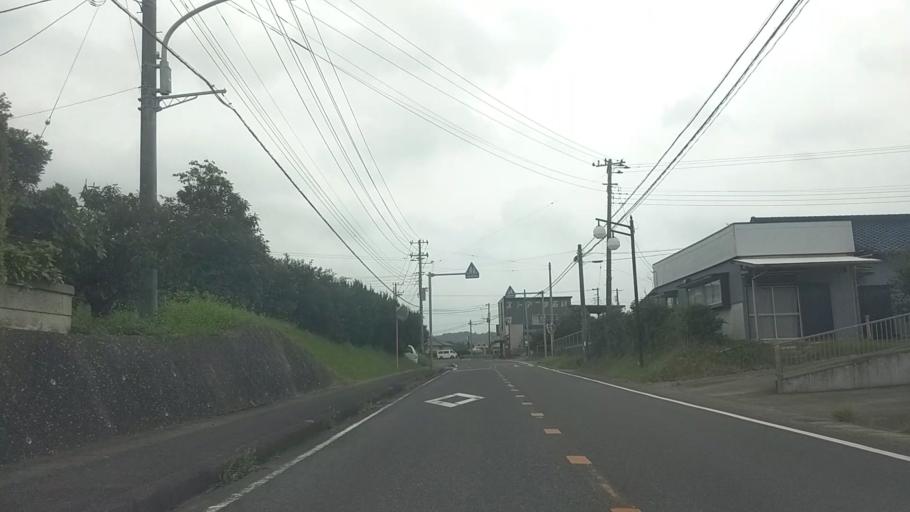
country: JP
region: Chiba
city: Kimitsu
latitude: 35.2169
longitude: 139.8960
